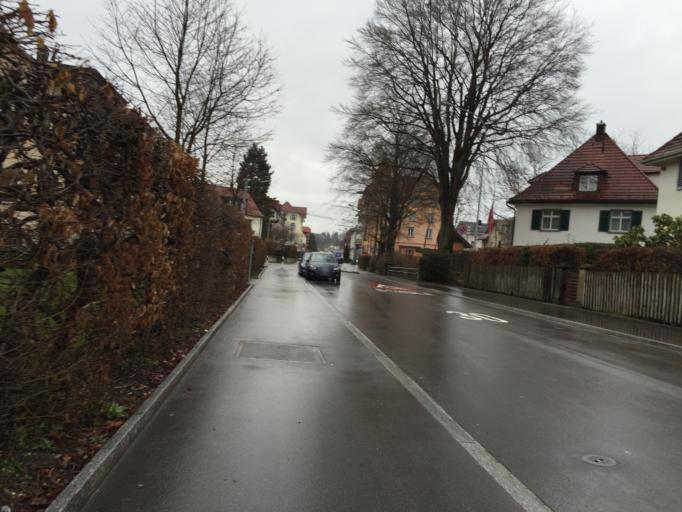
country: CH
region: Saint Gallen
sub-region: Wahlkreis St. Gallen
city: Sankt Gallen
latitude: 47.4364
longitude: 9.3767
